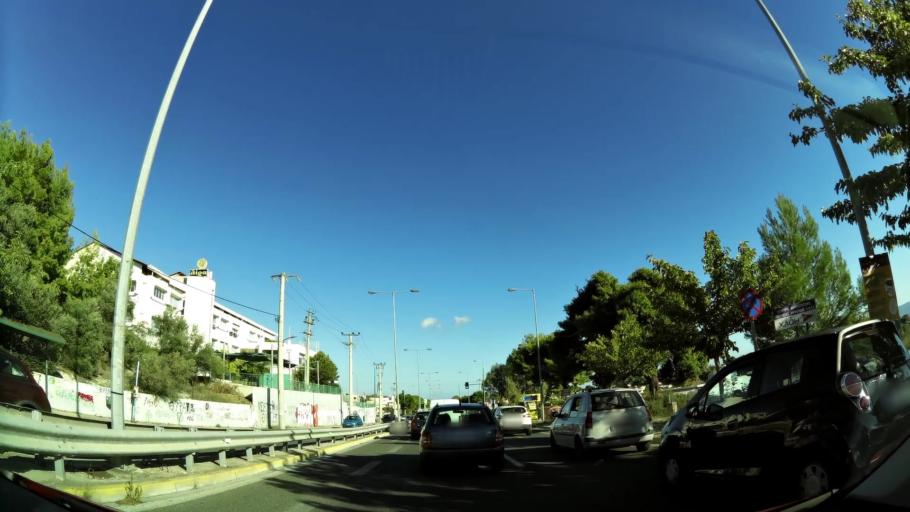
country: GR
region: Attica
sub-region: Nomarchia Anatolikis Attikis
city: Pallini
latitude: 38.0033
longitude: 23.8987
